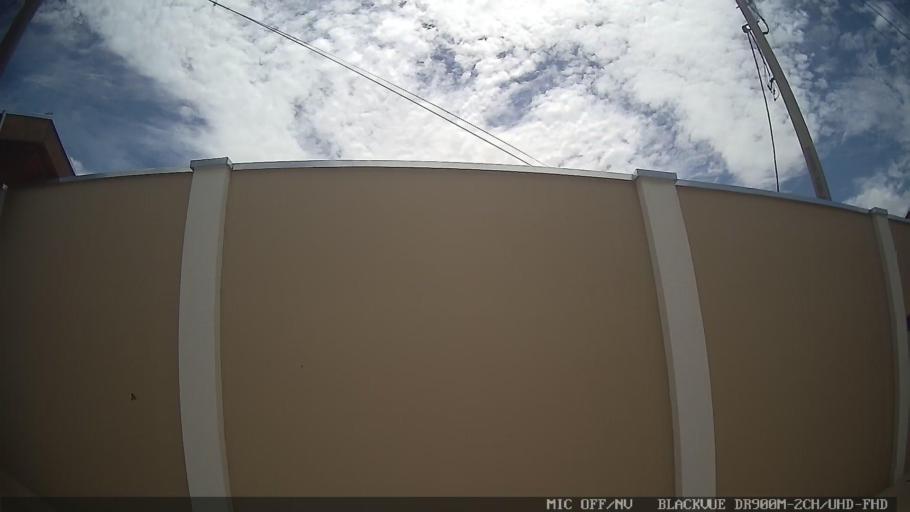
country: BR
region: Sao Paulo
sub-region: Conchas
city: Conchas
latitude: -23.0723
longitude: -47.9775
